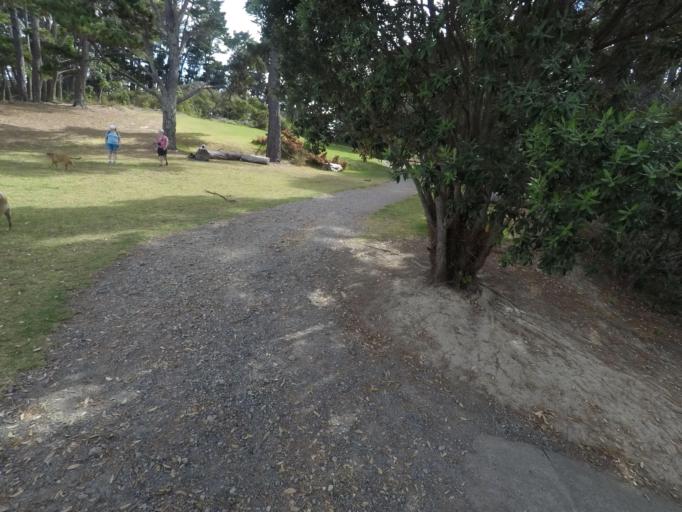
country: NZ
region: Auckland
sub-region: Auckland
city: North Shore
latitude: -36.8161
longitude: 174.6954
